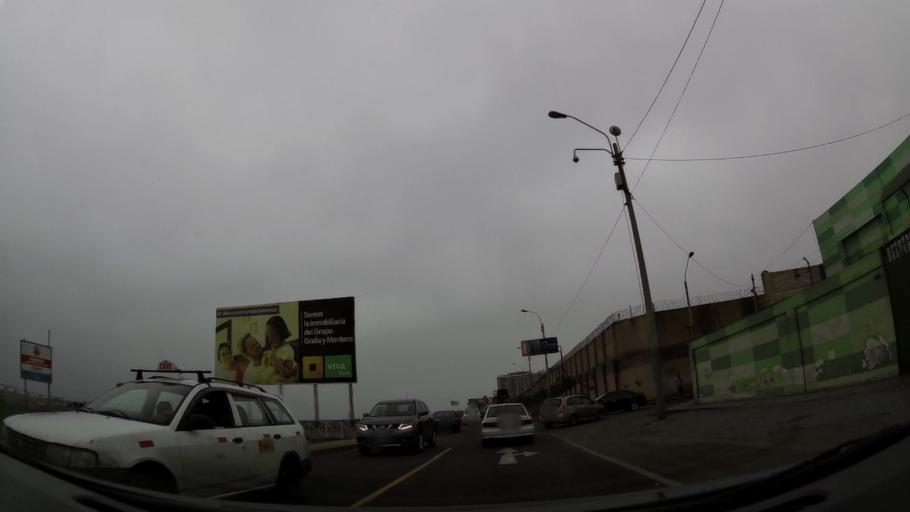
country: PE
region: Callao
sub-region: Callao
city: Callao
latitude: -12.0845
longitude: -77.0988
